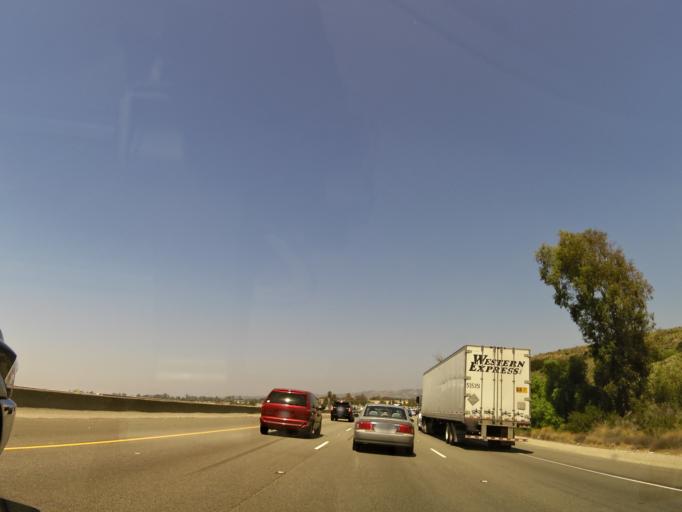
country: US
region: California
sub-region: Ventura County
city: Camarillo
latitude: 34.2063
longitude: -118.9906
